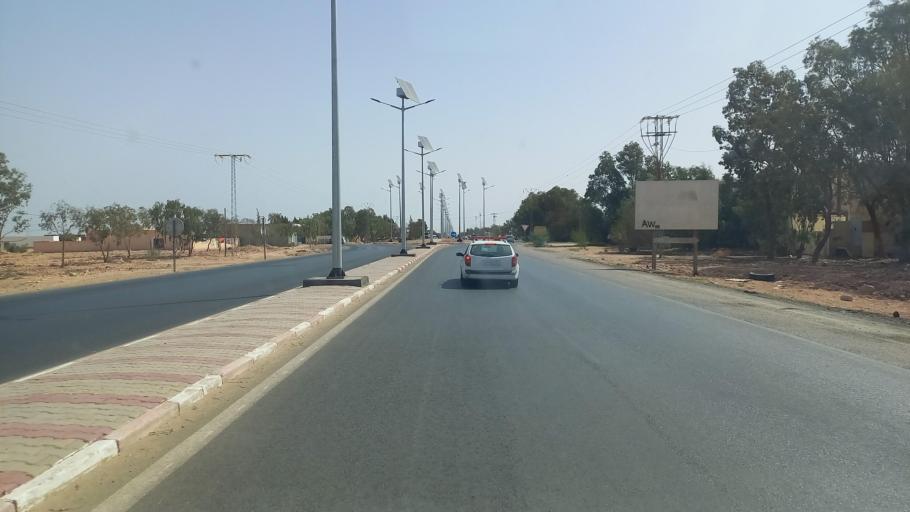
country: TN
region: Madanin
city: Medenine
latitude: 33.3514
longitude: 10.5316
